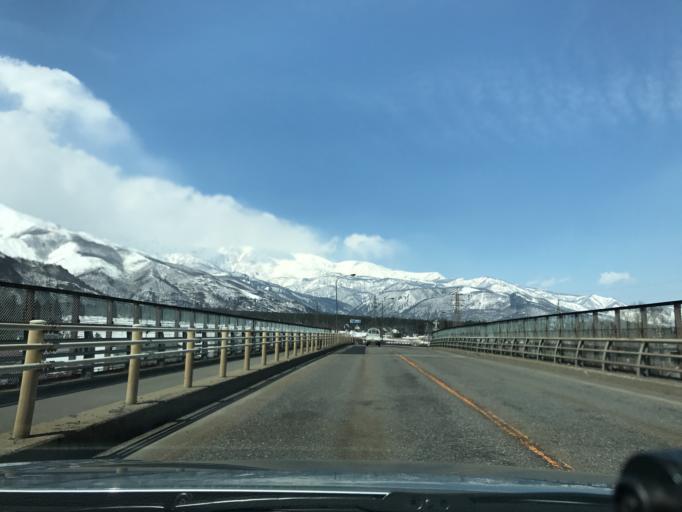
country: JP
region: Nagano
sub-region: Kitaazumi Gun
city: Hakuba
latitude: 36.6711
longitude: 137.8505
